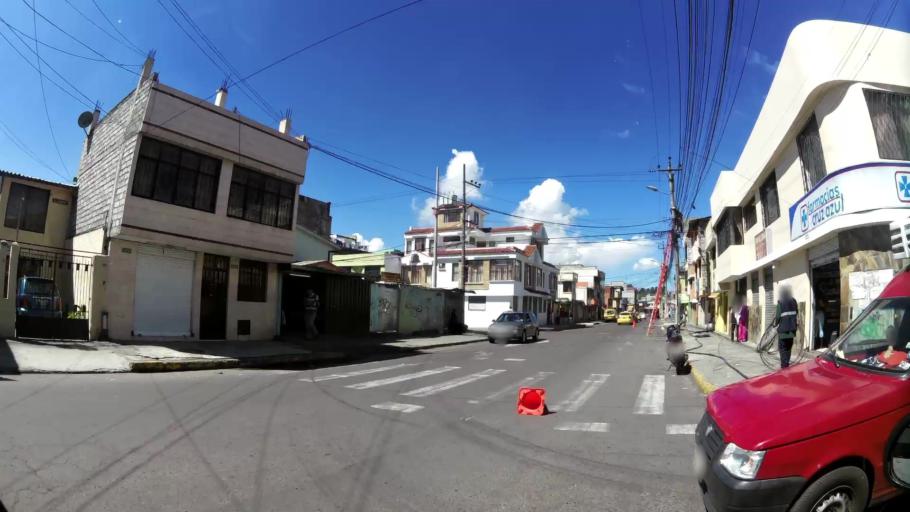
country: EC
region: Pichincha
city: Quito
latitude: -0.2558
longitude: -78.5343
